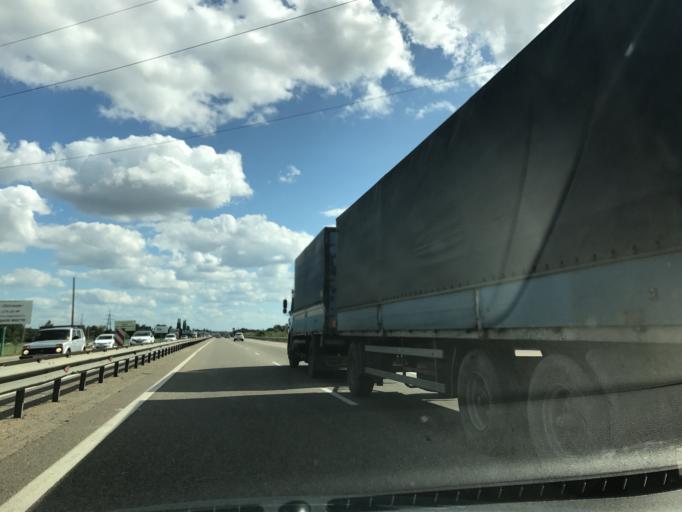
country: RU
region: Adygeya
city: Adygeysk
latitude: 44.9270
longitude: 39.1406
